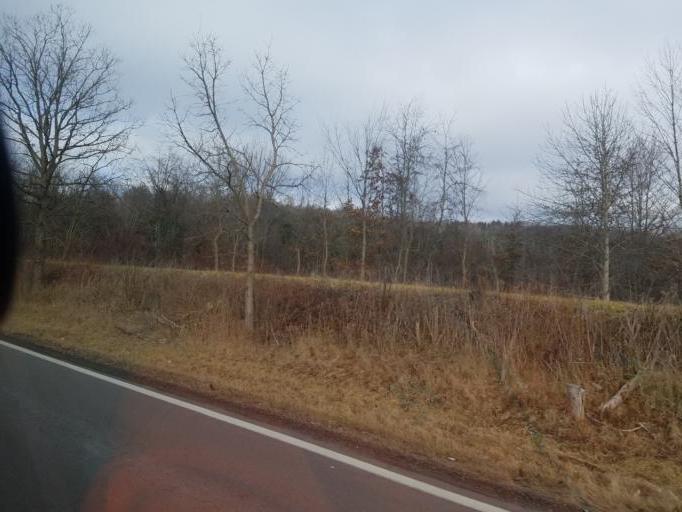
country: US
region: Ohio
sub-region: Sandusky County
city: Bellville
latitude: 40.6368
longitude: -82.5404
